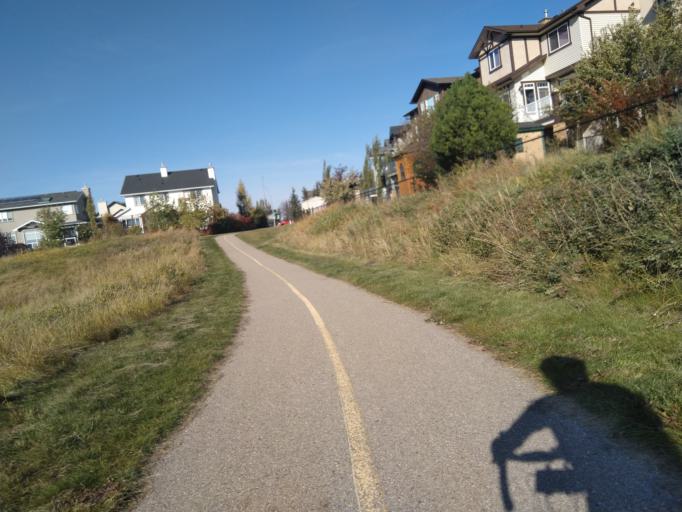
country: CA
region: Alberta
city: Calgary
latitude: 51.1589
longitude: -114.0973
